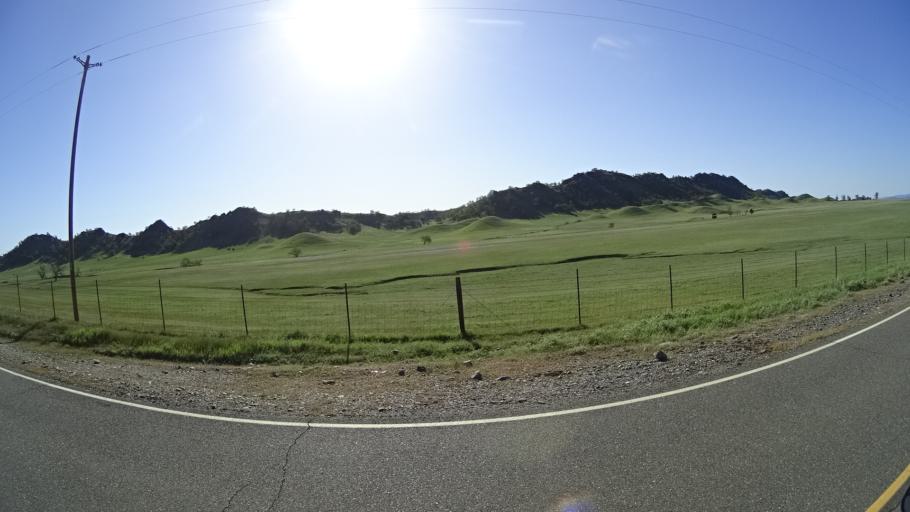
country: US
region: California
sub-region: Tehama County
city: Rancho Tehama Reserve
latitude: 39.7415
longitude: -122.5455
